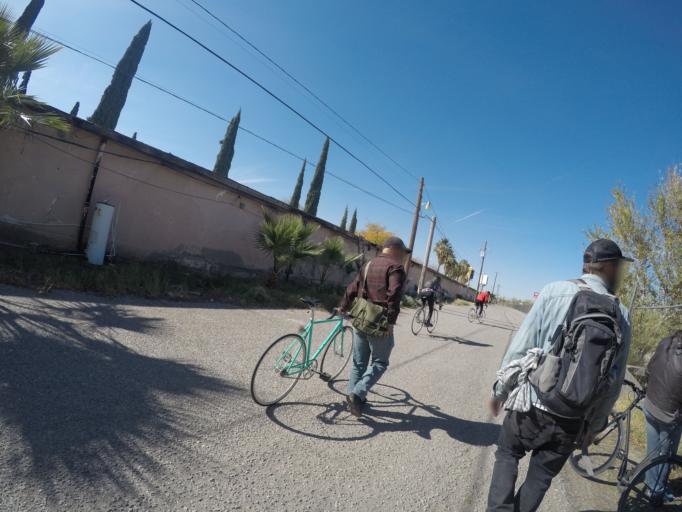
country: MX
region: Chihuahua
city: Ciudad Juarez
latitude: 31.7286
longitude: -106.4223
